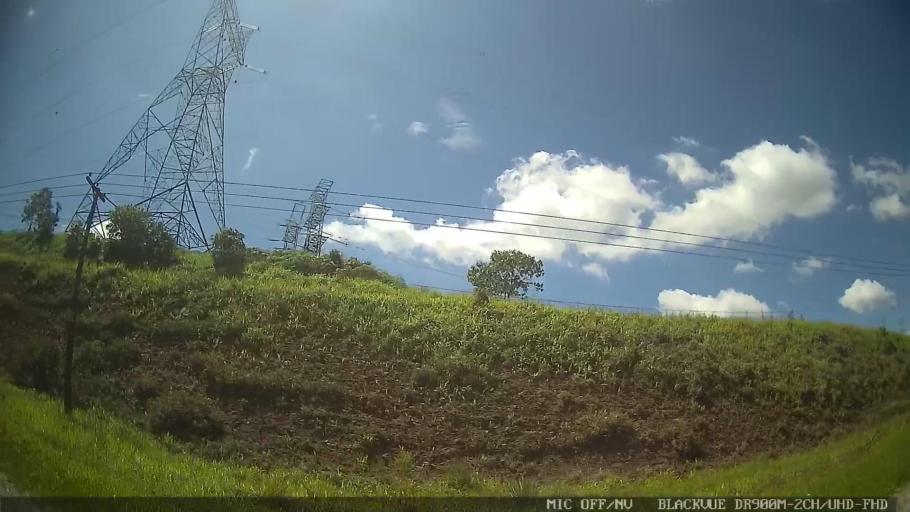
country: BR
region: Sao Paulo
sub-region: Mogi das Cruzes
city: Mogi das Cruzes
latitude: -23.6181
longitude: -46.1983
